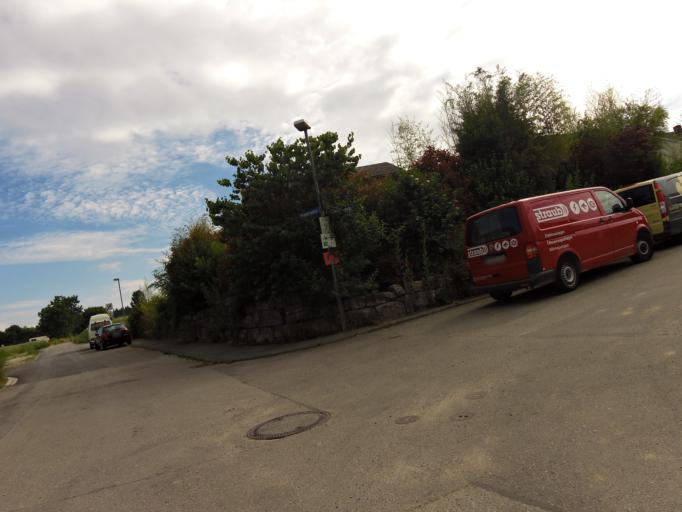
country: DE
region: Baden-Wuerttemberg
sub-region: Freiburg Region
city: Allensbach
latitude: 47.7221
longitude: 9.0524
